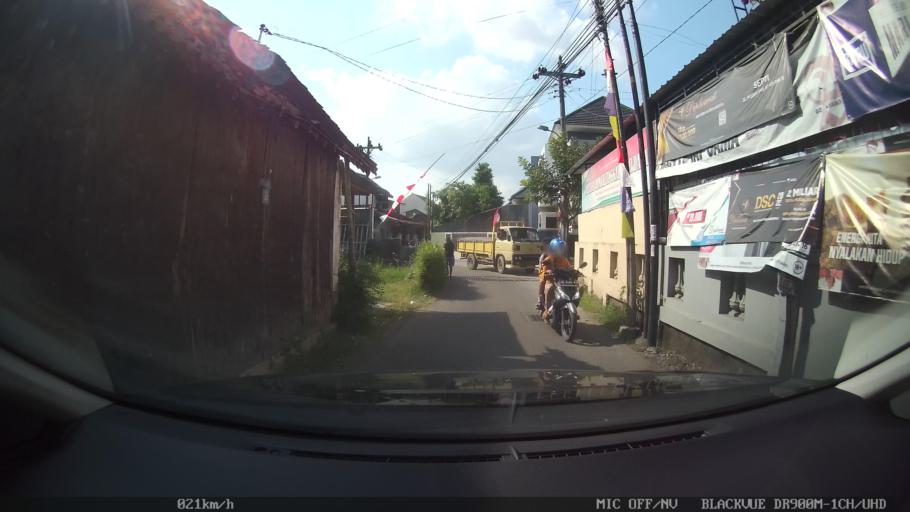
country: ID
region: Daerah Istimewa Yogyakarta
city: Sewon
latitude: -7.8328
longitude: 110.4019
